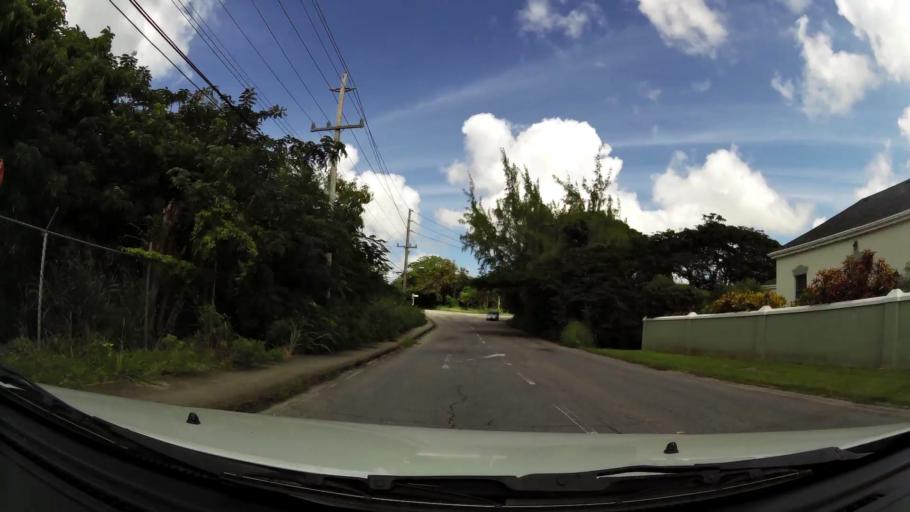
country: BB
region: Saint James
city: Holetown
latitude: 13.1479
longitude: -59.6231
